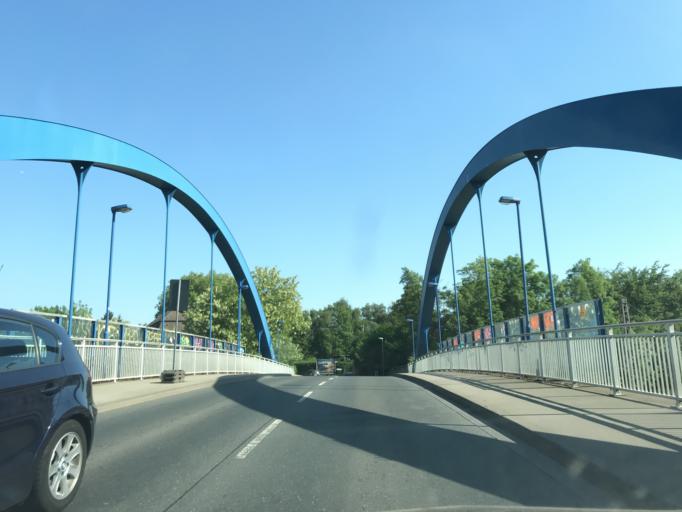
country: DE
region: North Rhine-Westphalia
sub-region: Regierungsbezirk Dusseldorf
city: Essen
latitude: 51.4674
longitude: 7.0725
